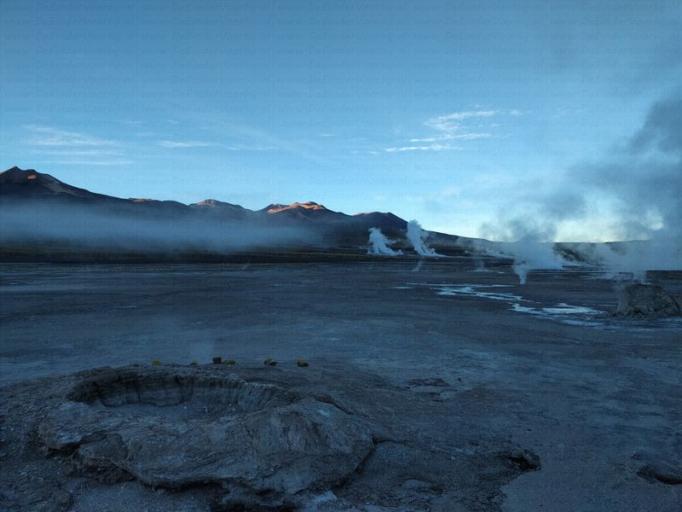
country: CL
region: Antofagasta
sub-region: Provincia de El Loa
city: San Pedro de Atacama
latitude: -22.3313
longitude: -68.0117
